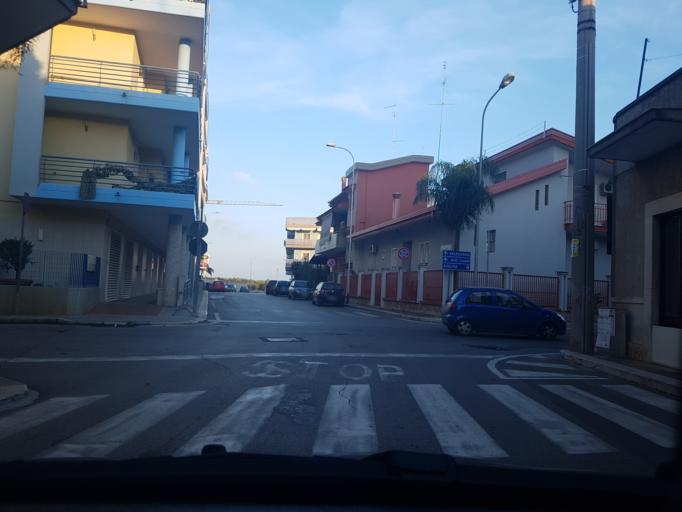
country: IT
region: Apulia
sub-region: Provincia di Bari
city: Bitritto
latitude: 41.0383
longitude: 16.8288
